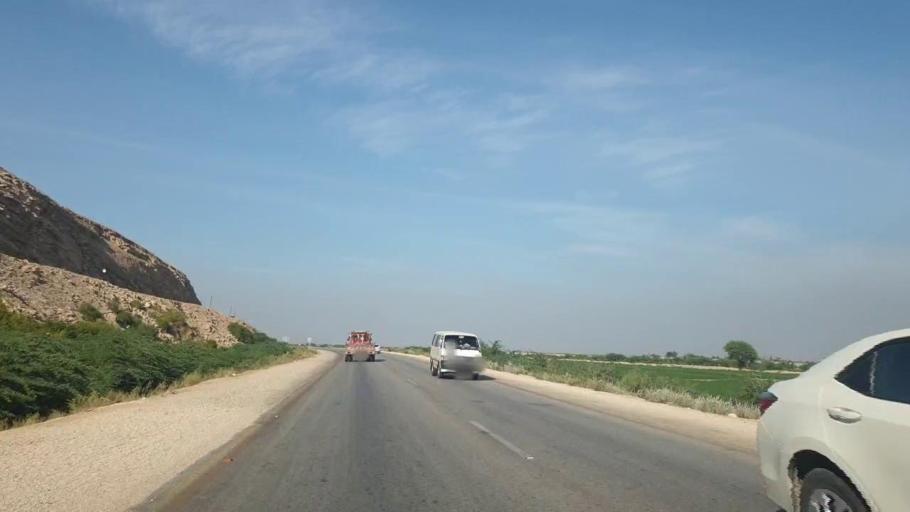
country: PK
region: Sindh
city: Sehwan
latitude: 26.3609
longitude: 67.8736
